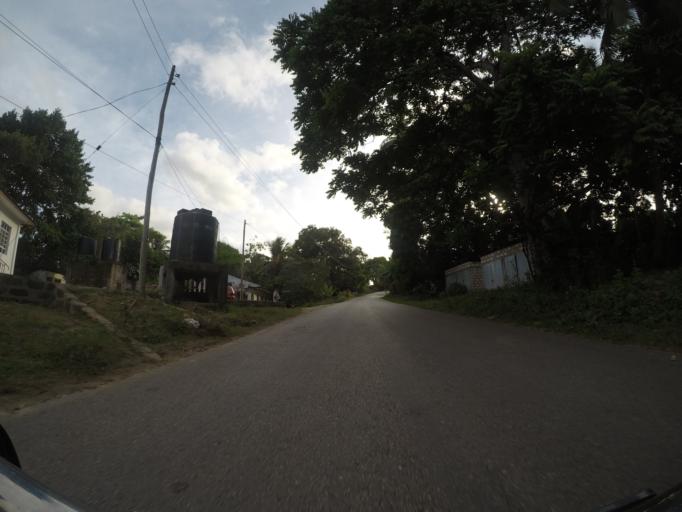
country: TZ
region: Pemba South
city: Chake Chake
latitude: -5.2782
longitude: 39.7684
